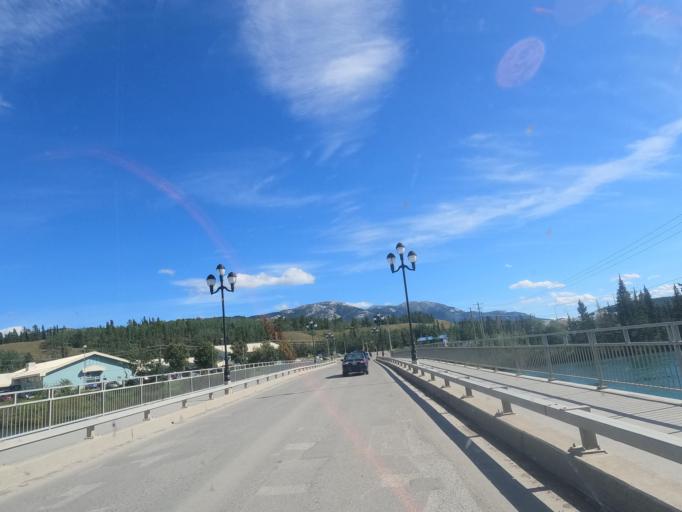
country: CA
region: Yukon
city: Whitehorse
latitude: 60.7140
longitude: -135.0459
